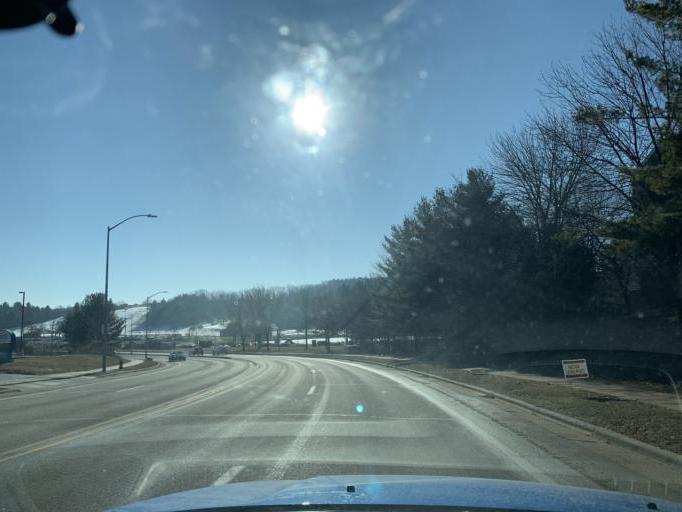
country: US
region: Wisconsin
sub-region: Dane County
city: Middleton
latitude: 43.0406
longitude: -89.5050
